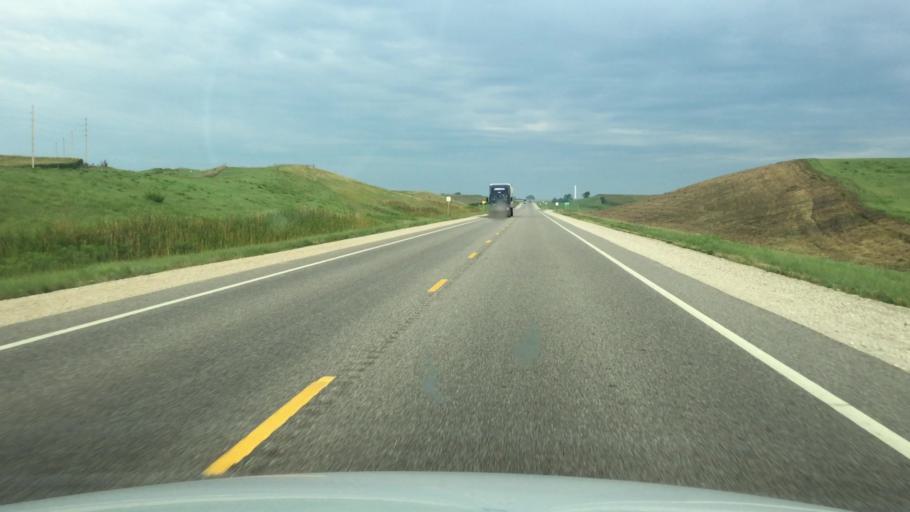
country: US
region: Kansas
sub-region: Doniphan County
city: Highland
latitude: 39.8422
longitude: -95.3170
